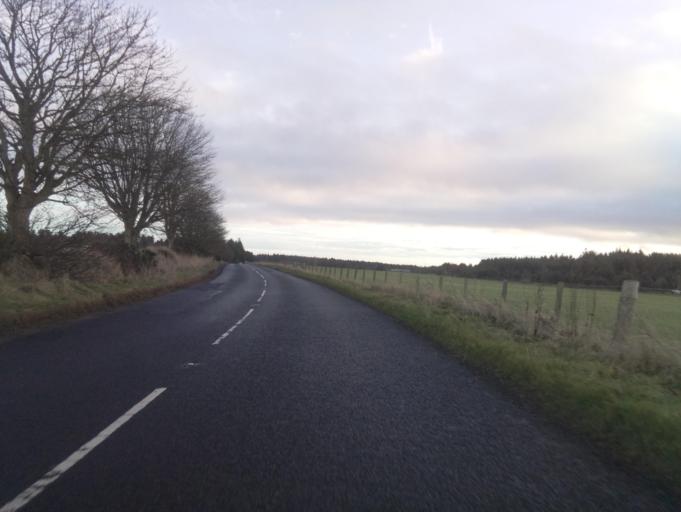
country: GB
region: Scotland
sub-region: Angus
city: Letham
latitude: 56.5596
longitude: -2.7695
